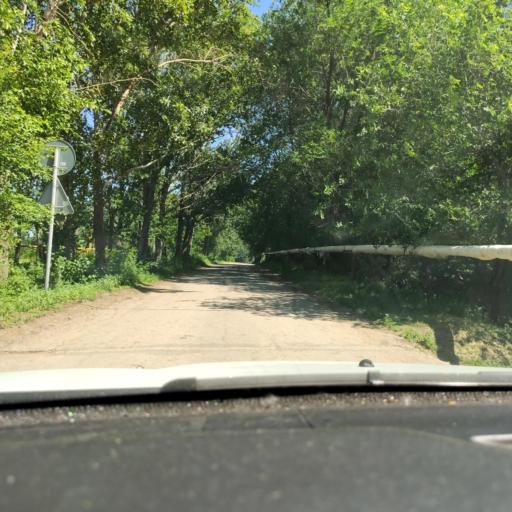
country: RU
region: Samara
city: Dubovyy Umet
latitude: 53.0358
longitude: 50.2473
